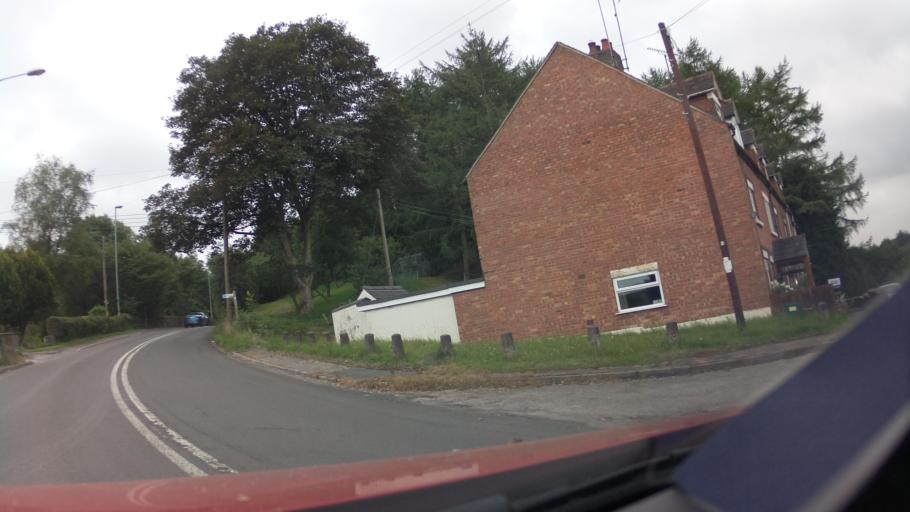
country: GB
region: England
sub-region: Staffordshire
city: Cheadle
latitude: 53.0217
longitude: -1.9651
